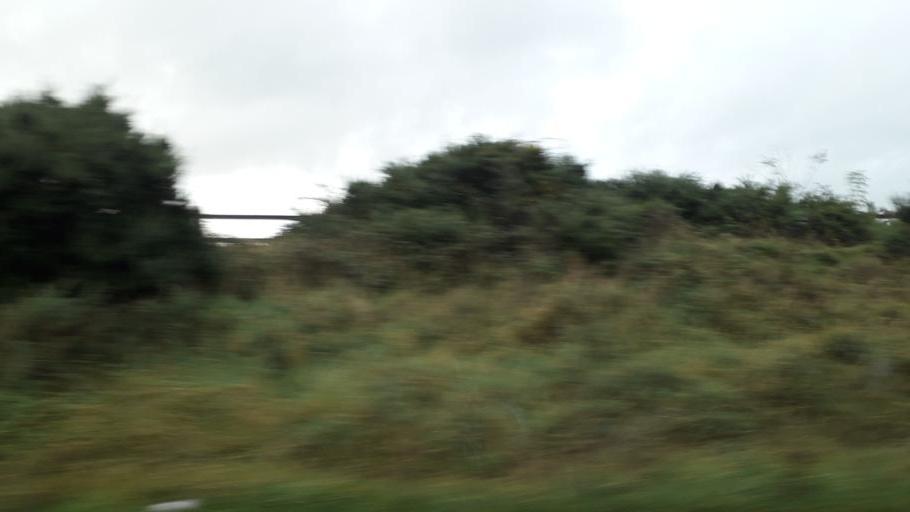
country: IE
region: Leinster
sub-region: An Longfort
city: Lanesborough
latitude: 53.7652
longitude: -8.0440
